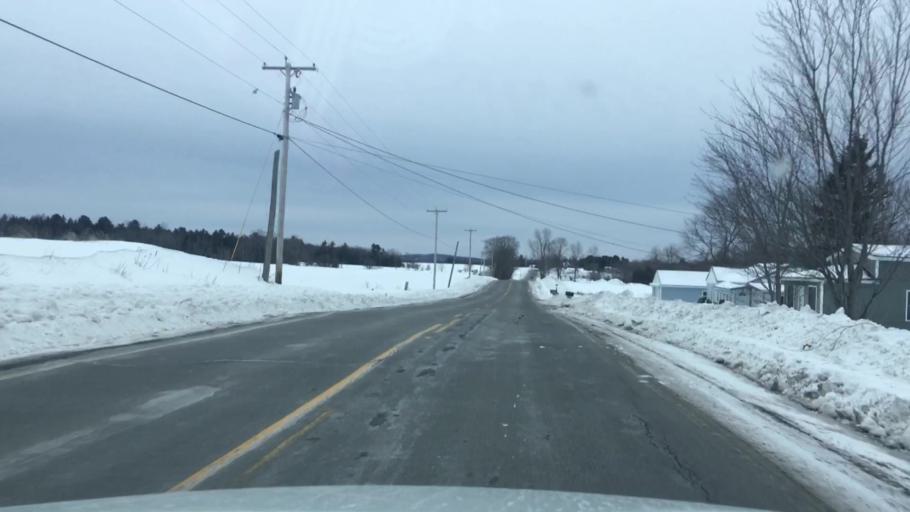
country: US
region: Maine
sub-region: Penobscot County
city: Corinna
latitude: 44.9365
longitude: -69.2328
